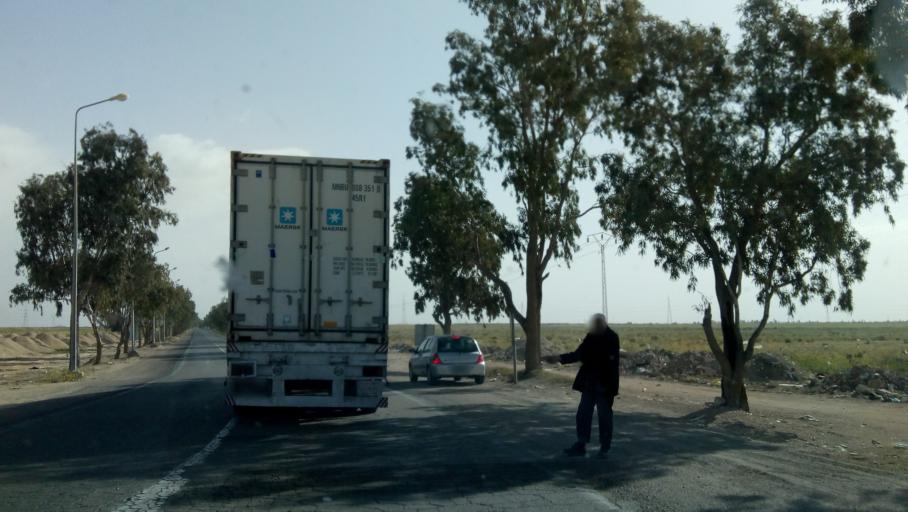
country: TN
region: Qabis
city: Gabes
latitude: 33.8880
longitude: 10.0224
